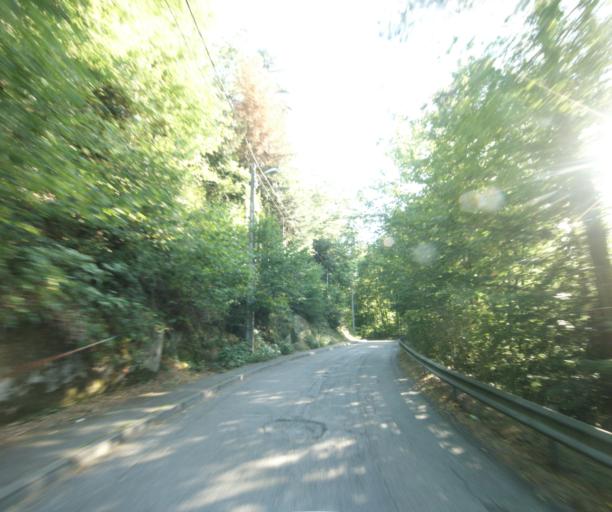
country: FR
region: Lorraine
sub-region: Departement des Vosges
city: Chantraine
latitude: 48.1511
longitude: 6.4502
